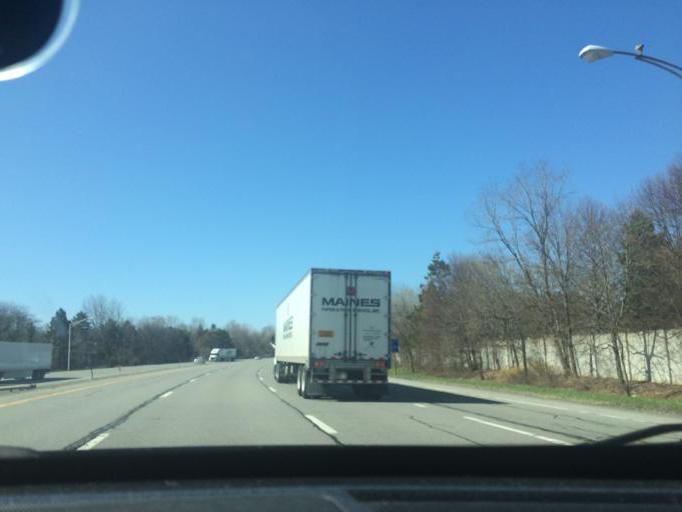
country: US
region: New York
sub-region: Monroe County
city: Brighton
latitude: 43.1116
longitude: -77.5532
